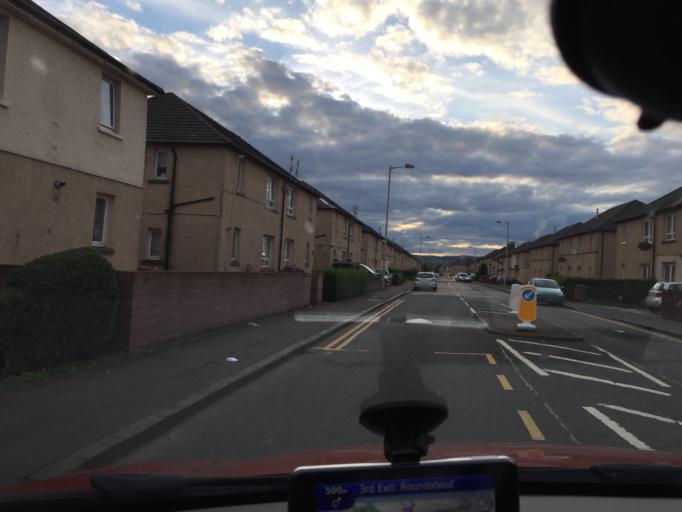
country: GB
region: Scotland
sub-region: Falkirk
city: Larbert
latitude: 56.0014
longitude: -3.8192
